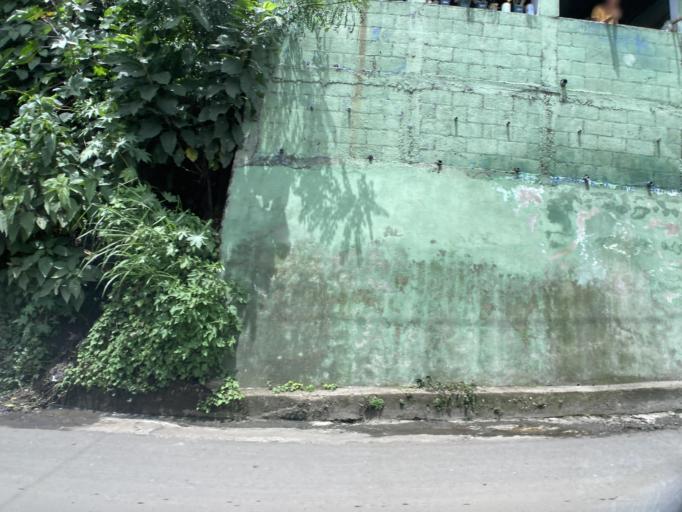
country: GT
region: Guatemala
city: Villa Canales
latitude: 14.4529
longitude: -90.5688
